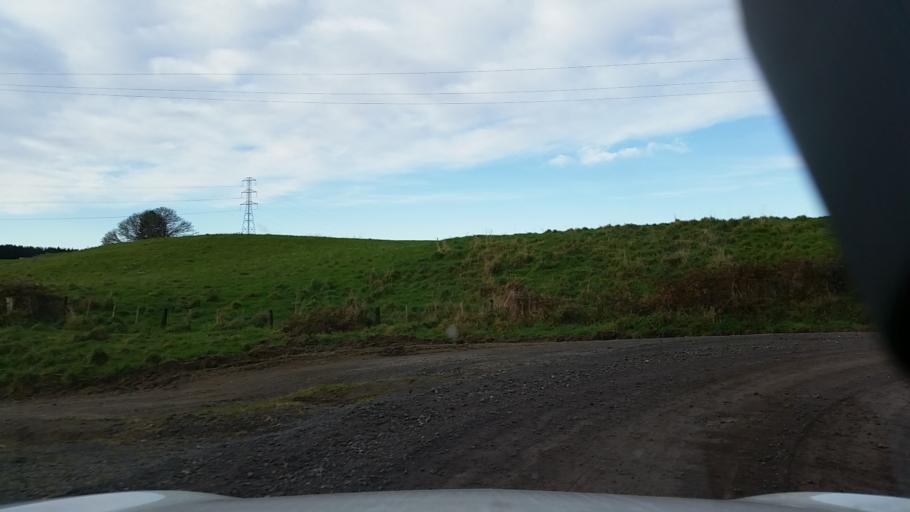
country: NZ
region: Bay of Plenty
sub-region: Rotorua District
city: Rotorua
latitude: -38.2272
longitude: 176.1628
